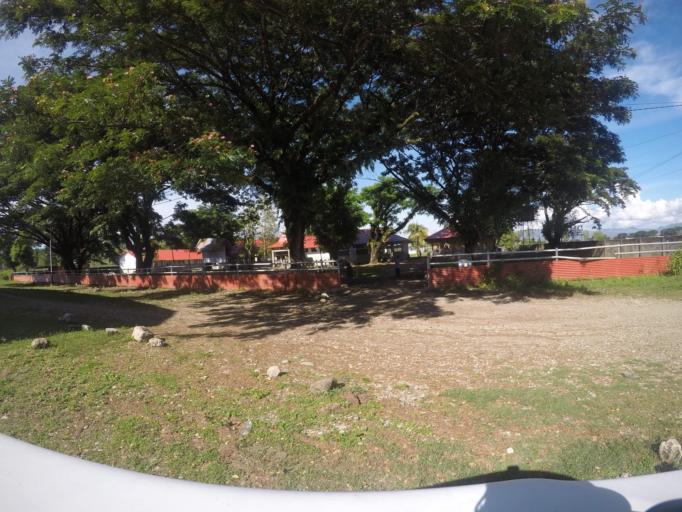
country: TL
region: Bobonaro
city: Maliana
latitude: -8.9941
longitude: 125.1911
